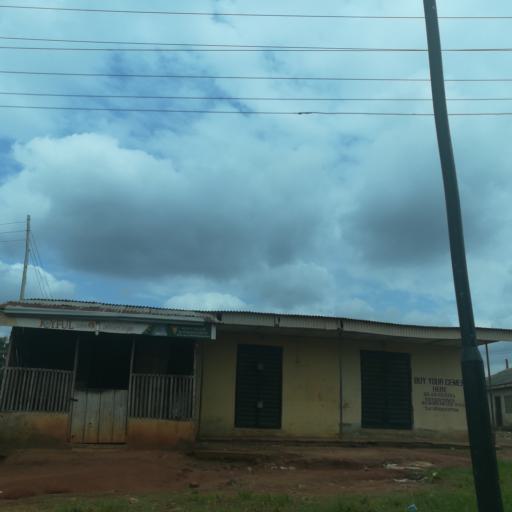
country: NG
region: Lagos
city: Ejirin
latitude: 6.6370
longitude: 3.7109
